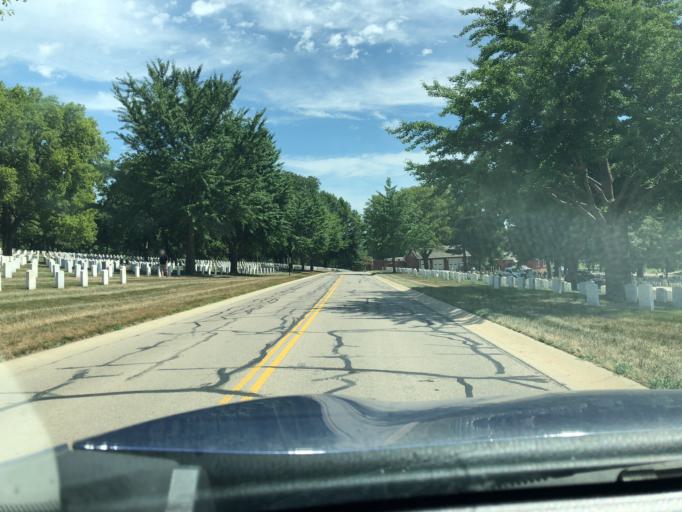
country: US
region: Kansas
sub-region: Leavenworth County
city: Leavenworth
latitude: 39.3506
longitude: -94.9315
